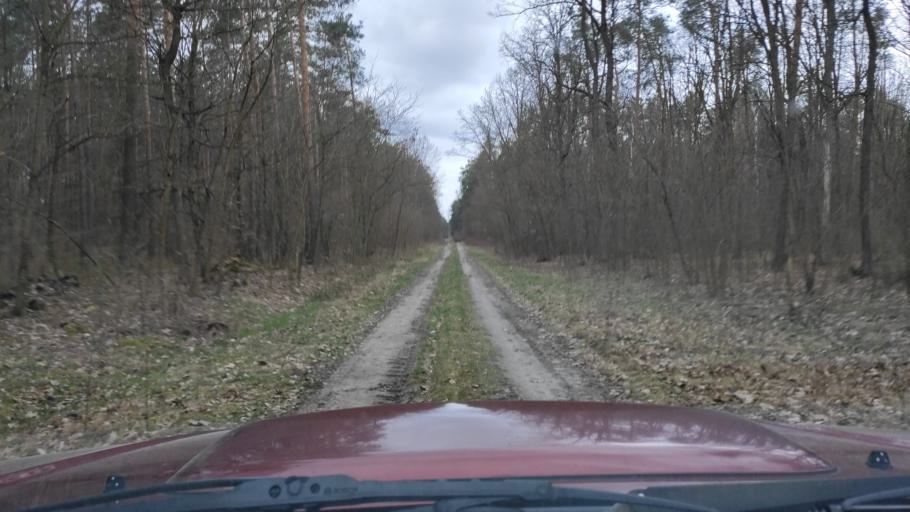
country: PL
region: Masovian Voivodeship
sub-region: Powiat kozienicki
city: Garbatka-Letnisko
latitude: 51.5060
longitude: 21.5562
